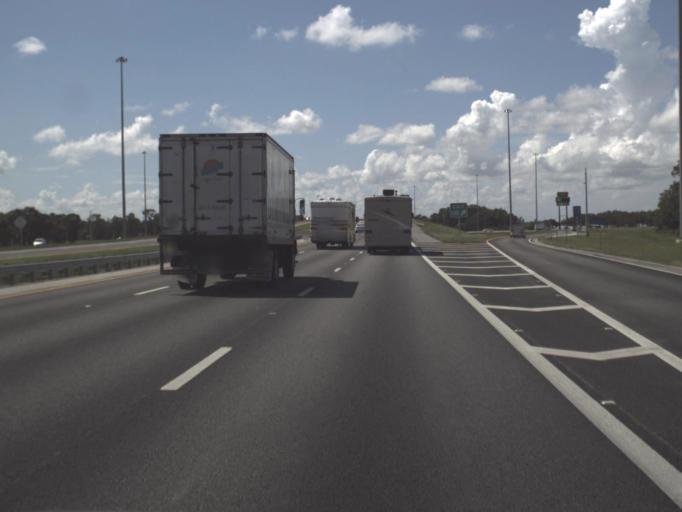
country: US
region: Florida
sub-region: Lee County
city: Tice
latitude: 26.6608
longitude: -81.7998
